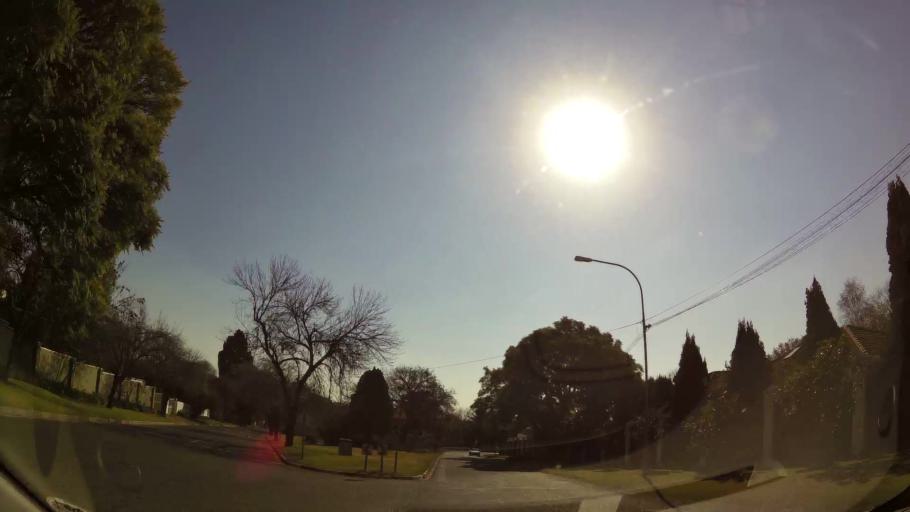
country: ZA
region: Gauteng
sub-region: City of Johannesburg Metropolitan Municipality
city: Johannesburg
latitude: -26.1364
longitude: 28.0305
